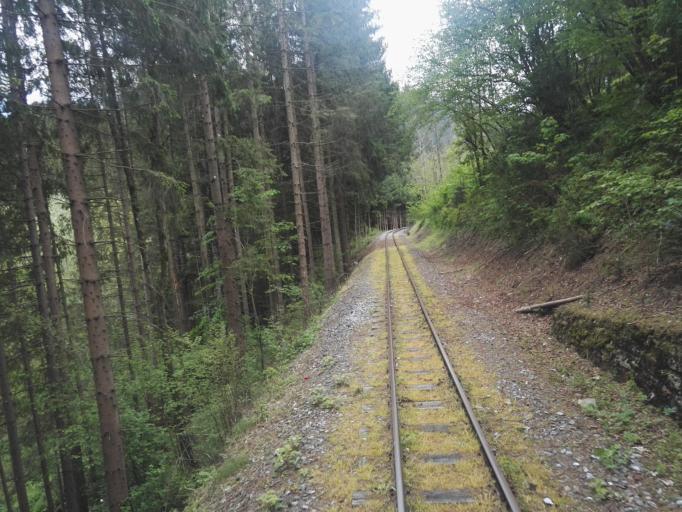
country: AT
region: Styria
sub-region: Politischer Bezirk Weiz
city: Birkfeld
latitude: 47.3472
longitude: 15.6993
